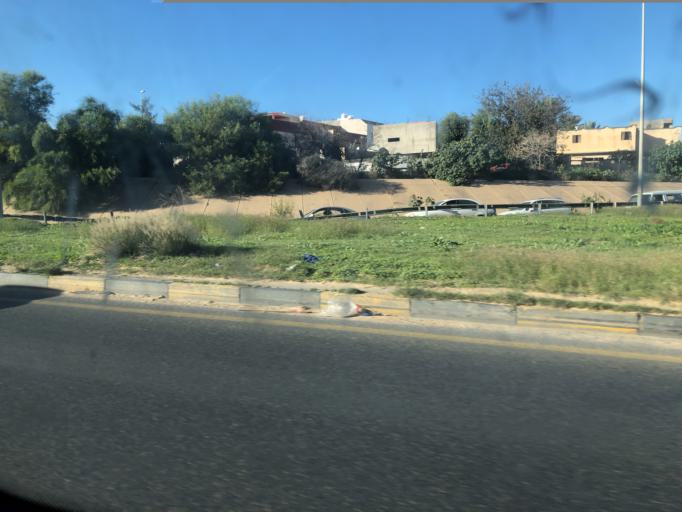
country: LY
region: Tripoli
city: Tripoli
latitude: 32.8689
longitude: 13.2453
